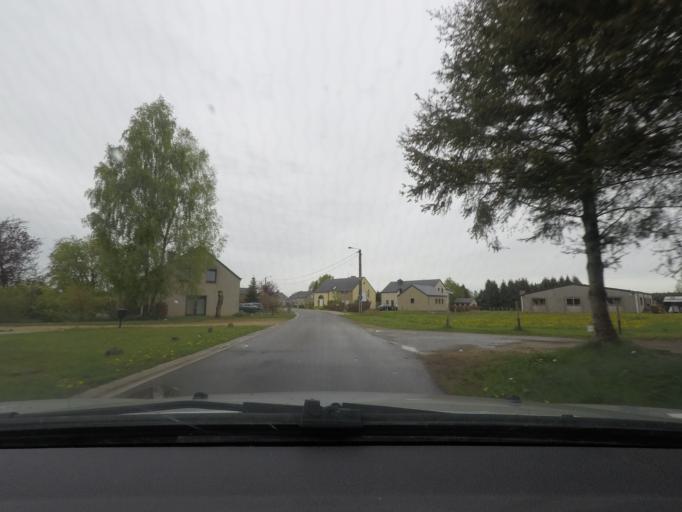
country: BE
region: Wallonia
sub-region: Province du Luxembourg
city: Etalle
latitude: 49.6632
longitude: 5.5604
